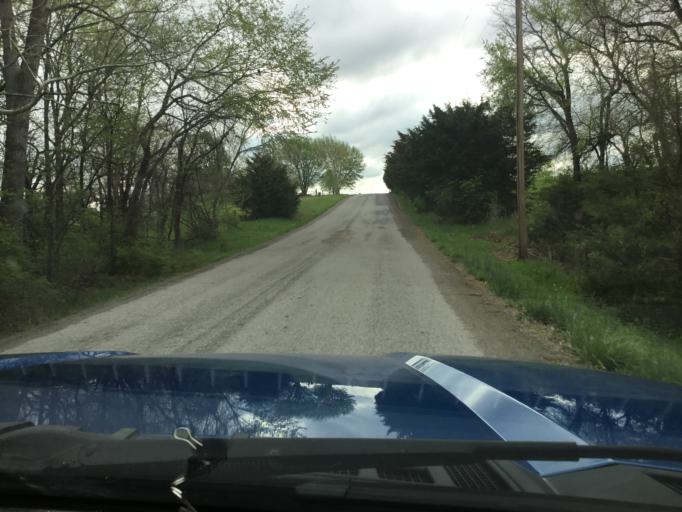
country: US
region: Kansas
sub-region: Douglas County
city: Lawrence
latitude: 38.9281
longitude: -95.1955
